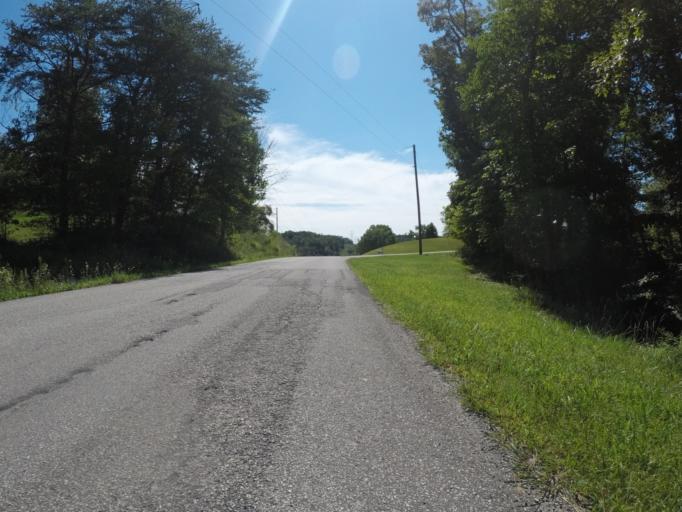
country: US
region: Kentucky
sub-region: Boyd County
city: Catlettsburg
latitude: 38.4047
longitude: -82.6514
